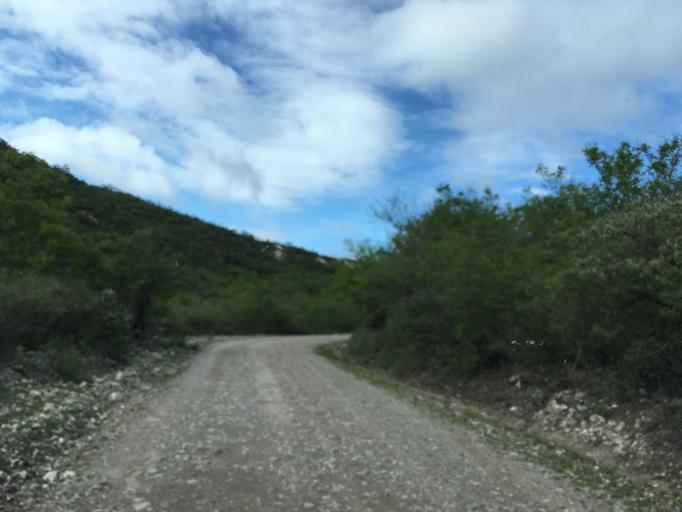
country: MX
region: Hidalgo
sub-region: Metztitlan
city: Fontezuelas
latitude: 20.6427
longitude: -98.9399
